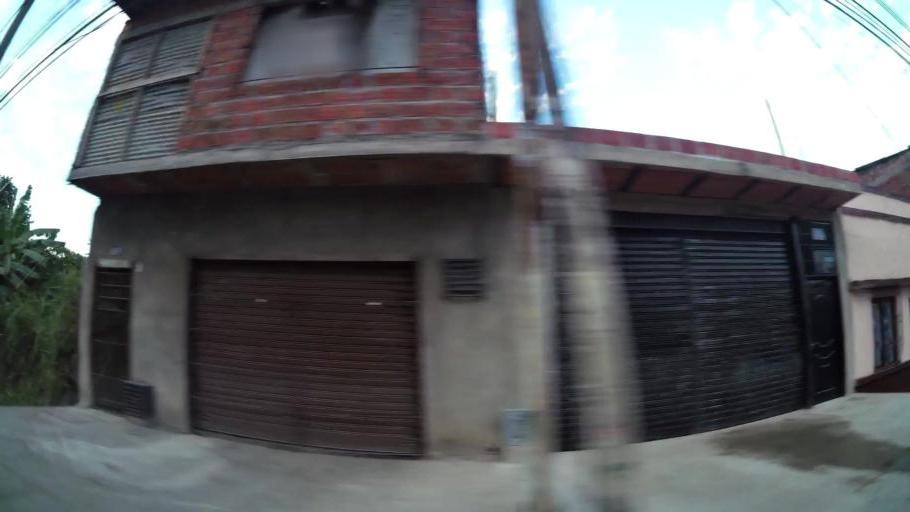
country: CO
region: Valle del Cauca
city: Cali
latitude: 3.4658
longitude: -76.5162
